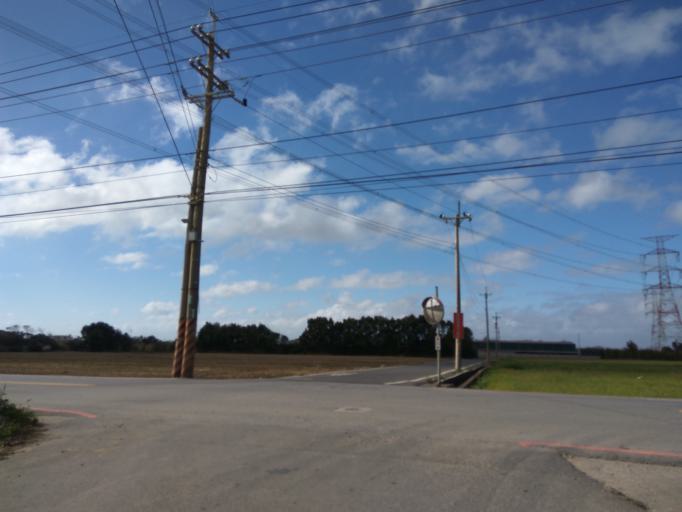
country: TW
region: Taiwan
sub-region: Hsinchu
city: Zhubei
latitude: 24.9729
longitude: 121.0755
